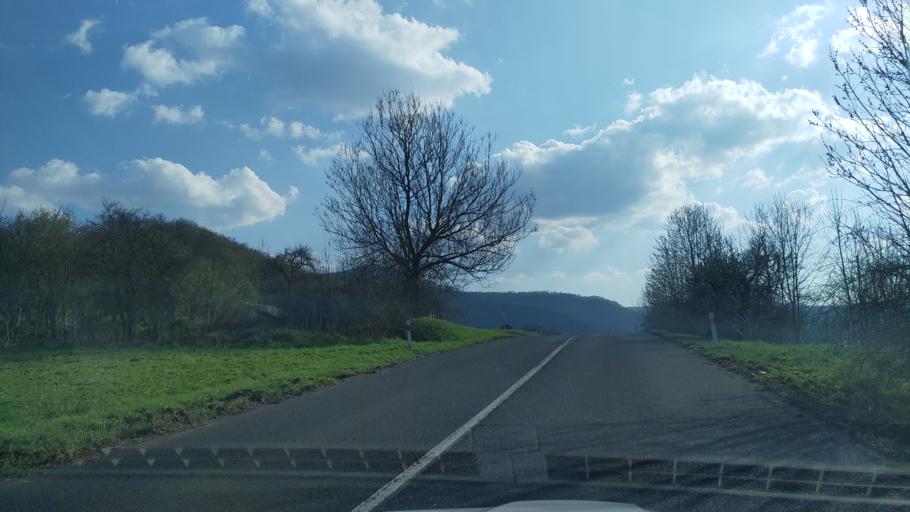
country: CZ
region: Ustecky
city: Povrly
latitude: 50.6783
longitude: 14.1758
